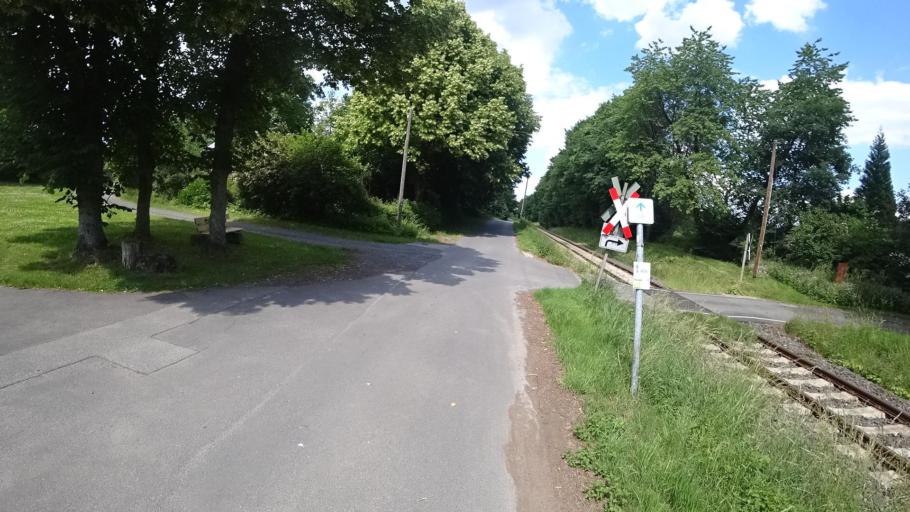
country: DE
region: Rheinland-Pfalz
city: Bachenberg
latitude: 50.7109
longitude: 7.6581
